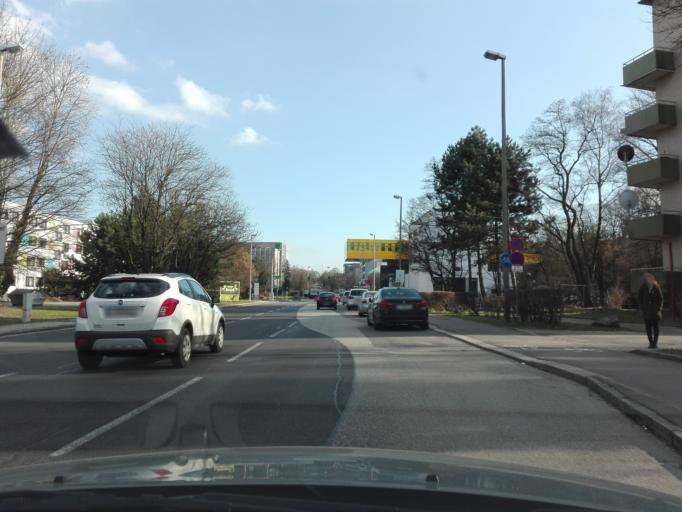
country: AT
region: Upper Austria
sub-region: Linz Stadt
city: Linz
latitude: 48.2814
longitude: 14.3037
